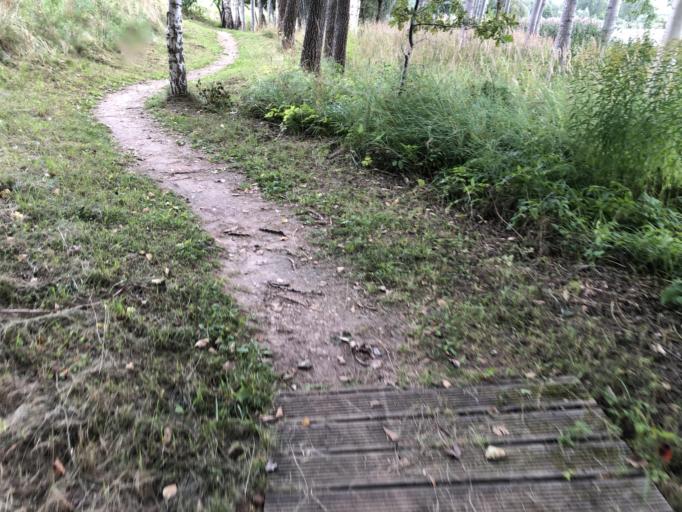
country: LV
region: Koknese
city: Koknese
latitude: 56.6394
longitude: 25.4454
